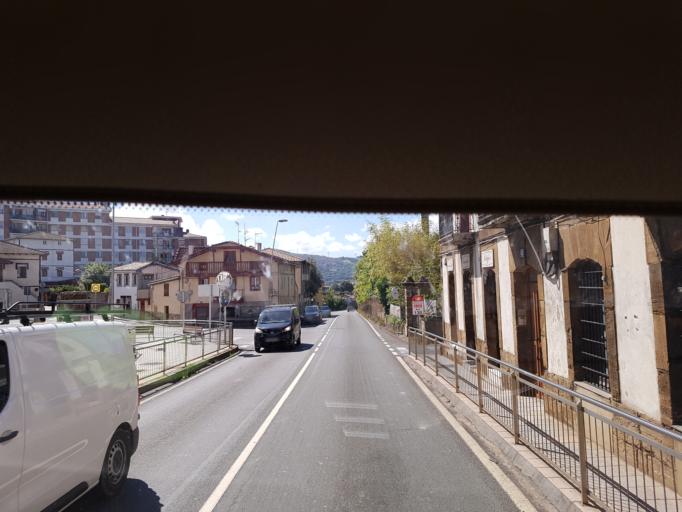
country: ES
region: Basque Country
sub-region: Bizkaia
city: San Julian de Muskiz
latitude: 43.3190
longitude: -3.0981
